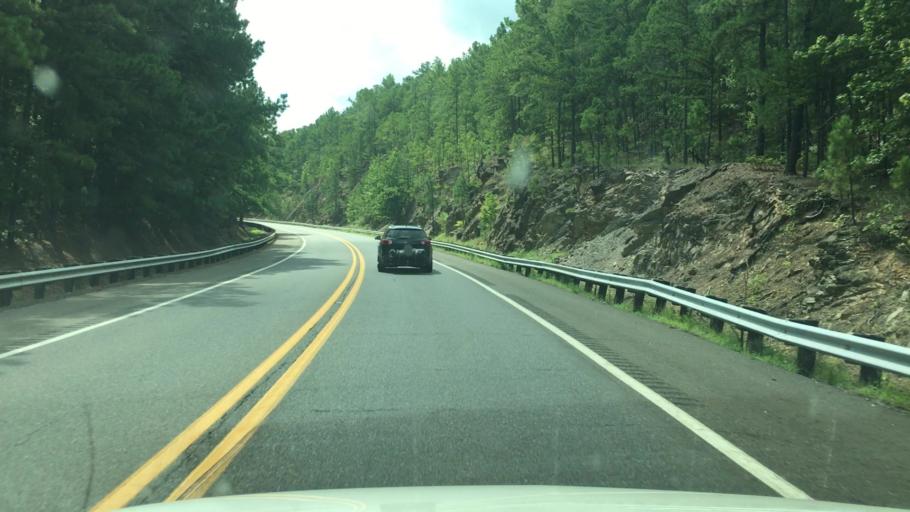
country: US
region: Arkansas
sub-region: Clark County
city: Arkadelphia
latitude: 34.2324
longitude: -93.0998
